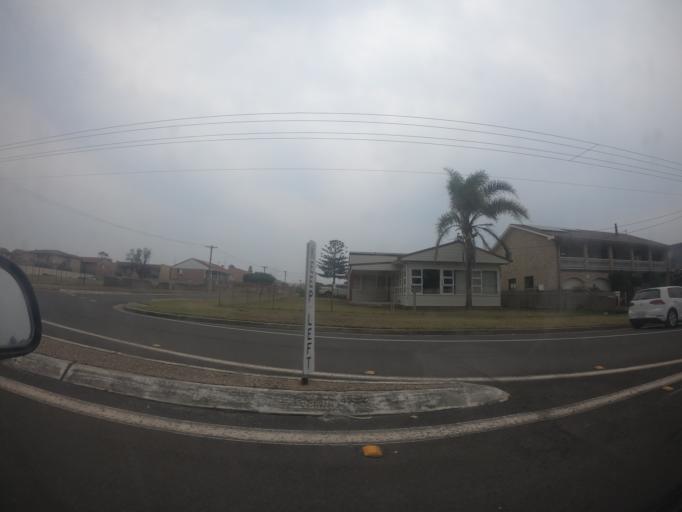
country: AU
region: New South Wales
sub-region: Shellharbour
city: Lake Illawarra
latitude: -34.5448
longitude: 150.8690
